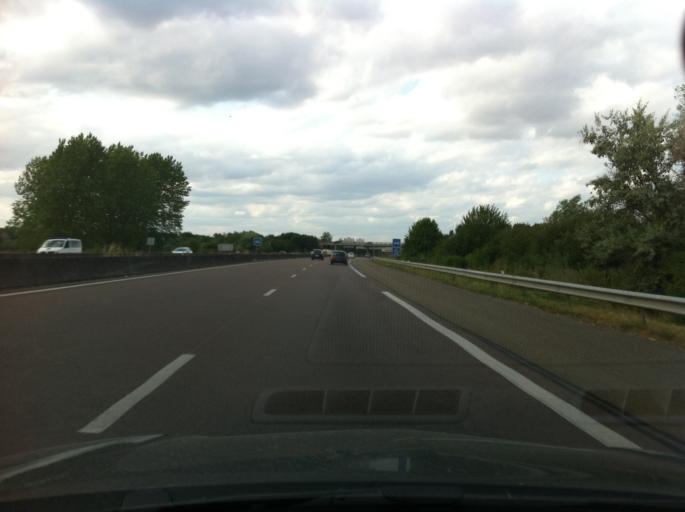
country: FR
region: Ile-de-France
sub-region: Departement de Seine-et-Marne
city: Lieusaint
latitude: 48.6311
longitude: 2.5363
